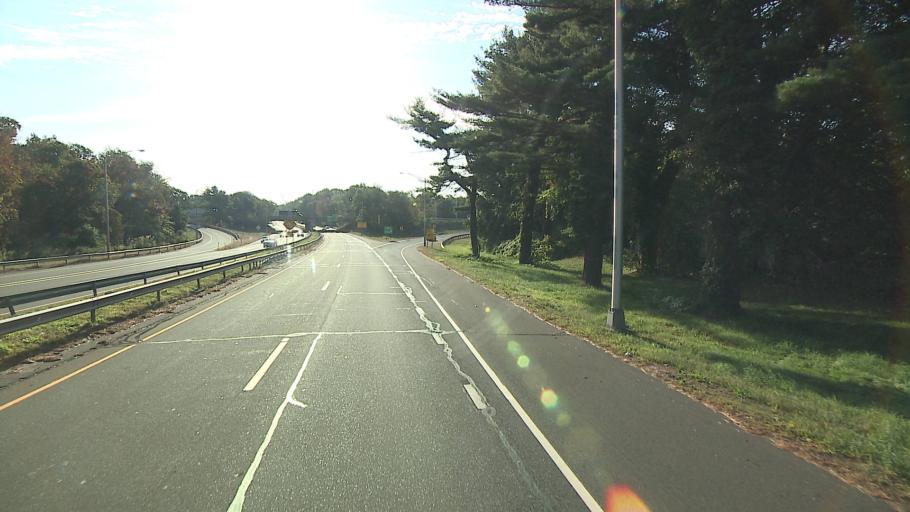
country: US
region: Connecticut
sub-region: New Haven County
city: City of Milford (balance)
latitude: 41.2344
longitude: -73.0716
